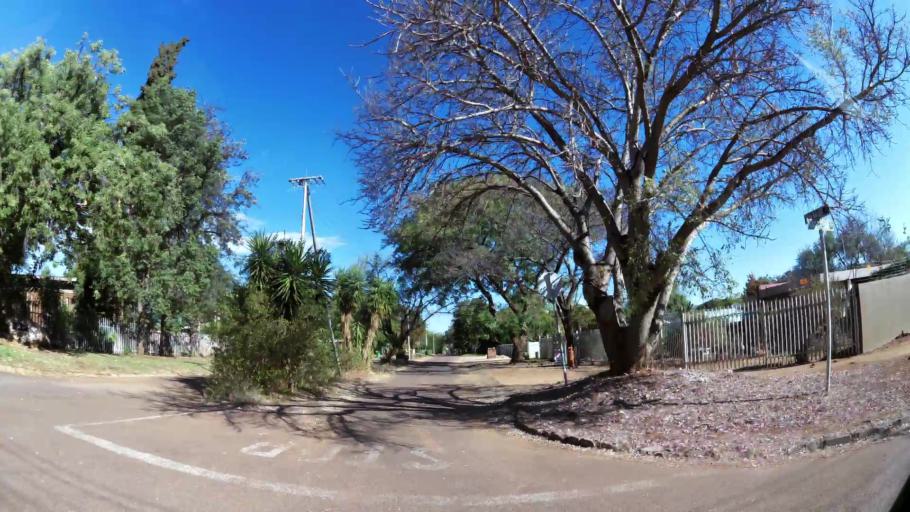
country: ZA
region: Limpopo
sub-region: Waterberg District Municipality
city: Mokopane
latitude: -24.2062
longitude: 29.0100
